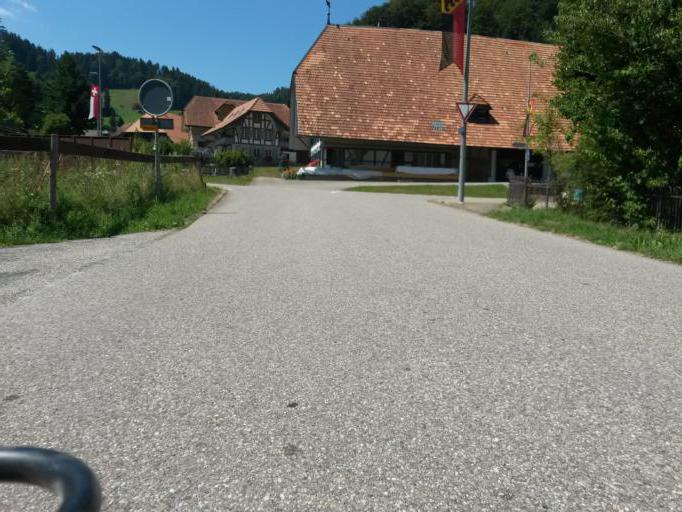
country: CH
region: Bern
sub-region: Emmental District
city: Lutzelfluh
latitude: 46.9955
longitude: 7.6566
